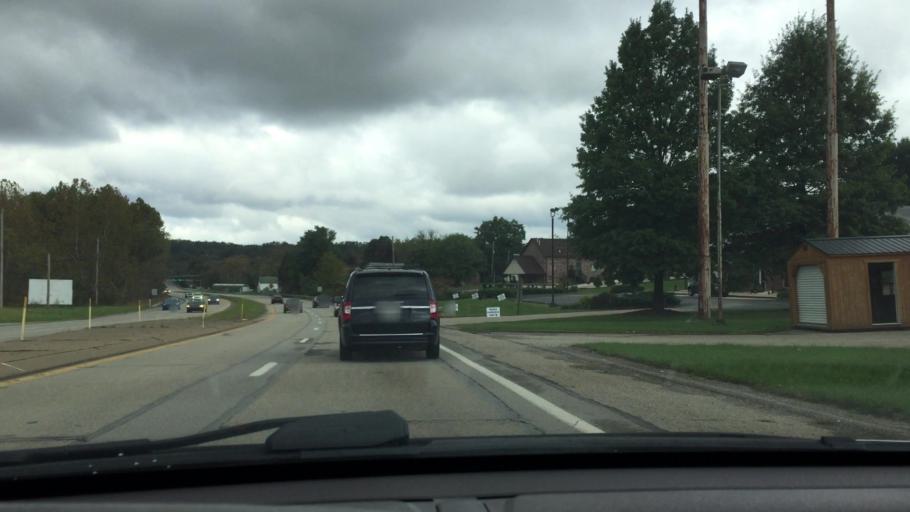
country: US
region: Pennsylvania
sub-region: Westmoreland County
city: Fellsburg
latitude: 40.1591
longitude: -79.7786
